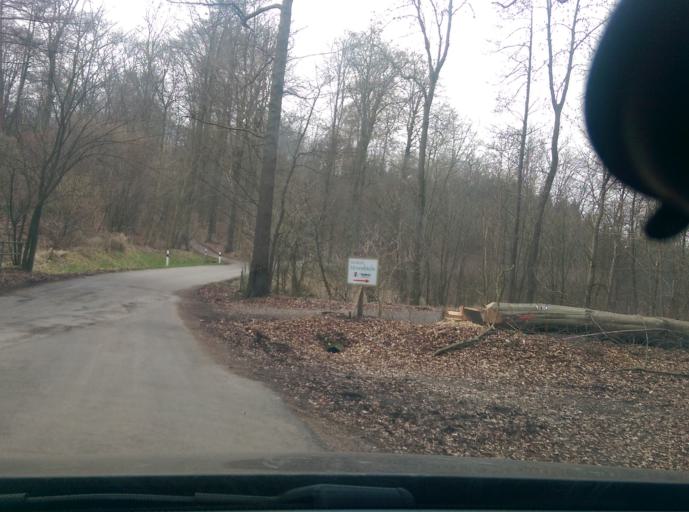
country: DE
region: Lower Saxony
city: Hameln
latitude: 52.1261
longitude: 9.3958
